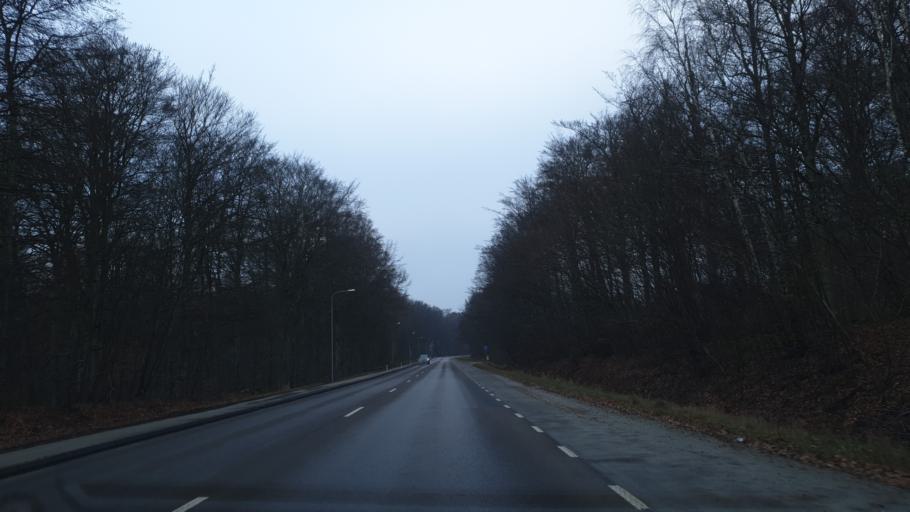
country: SE
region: Blekinge
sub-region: Solvesborgs Kommun
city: Soelvesborg
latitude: 56.0569
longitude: 14.5596
